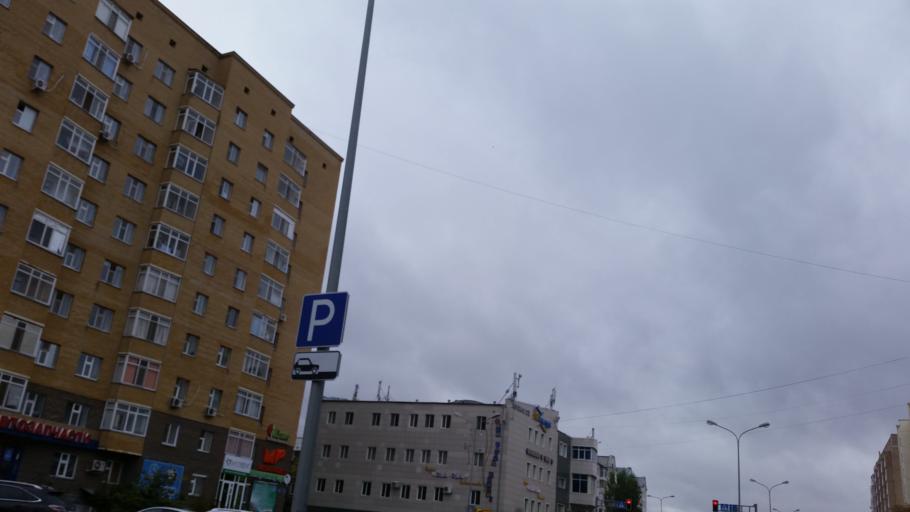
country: KZ
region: Astana Qalasy
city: Astana
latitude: 51.1524
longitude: 71.5008
